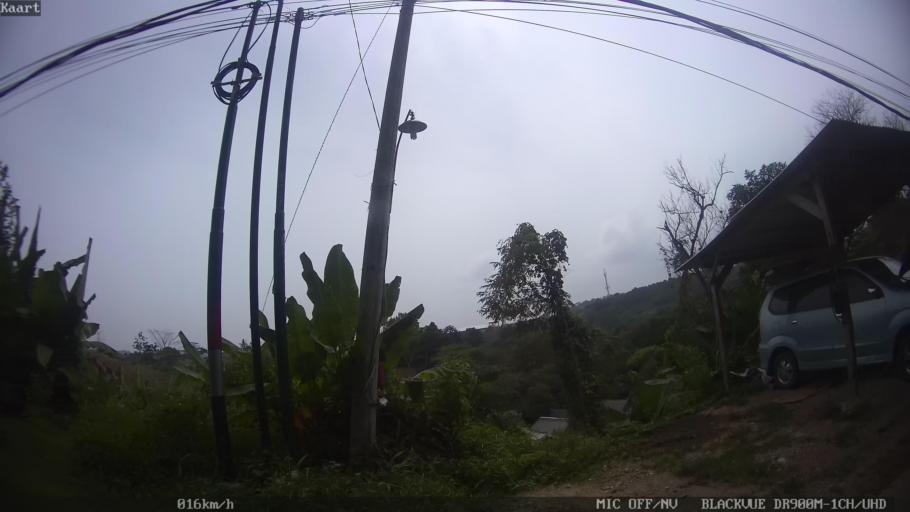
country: ID
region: Lampung
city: Panjang
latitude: -5.4387
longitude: 105.3149
